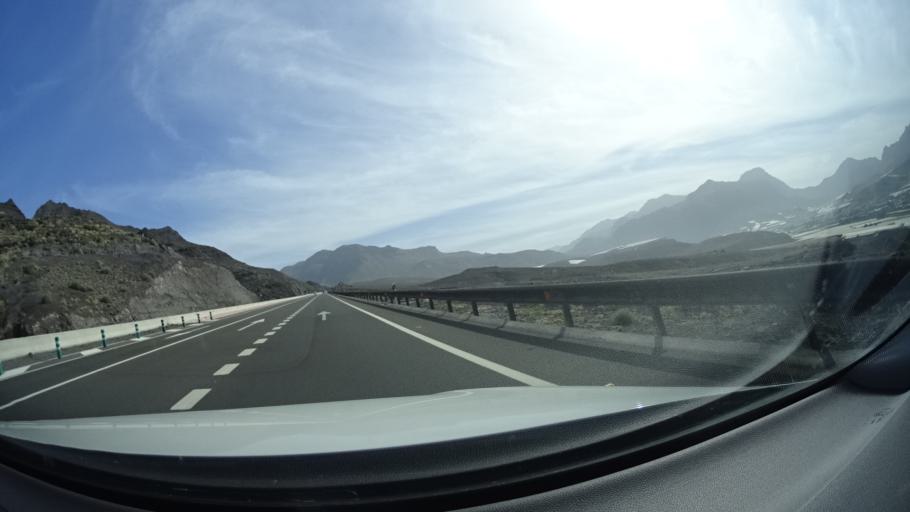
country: ES
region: Canary Islands
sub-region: Provincia de Las Palmas
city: San Nicolas
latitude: 28.0070
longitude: -15.8030
